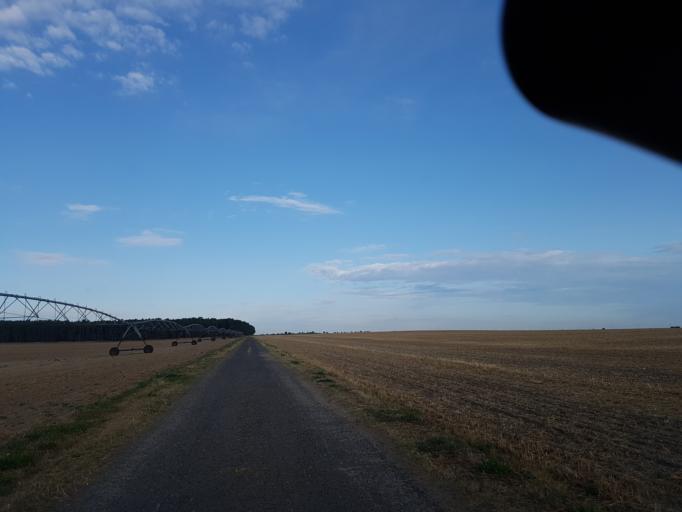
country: DE
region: Brandenburg
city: Niedergorsdorf
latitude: 51.9335
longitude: 13.0168
